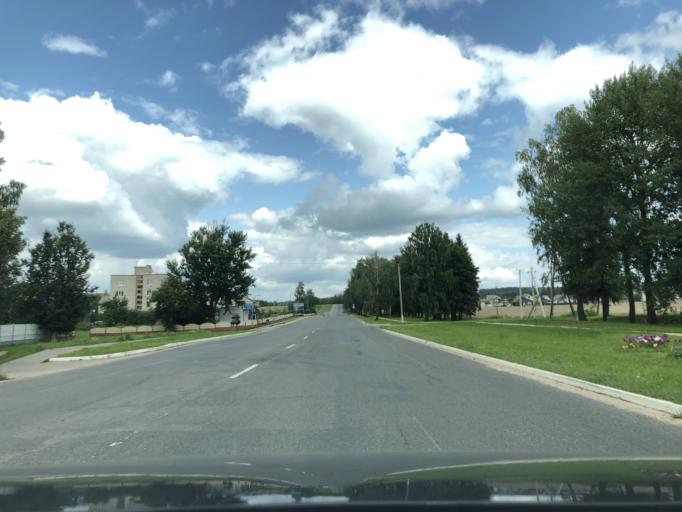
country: BY
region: Minsk
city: Lahoysk
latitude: 54.2189
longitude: 27.8512
